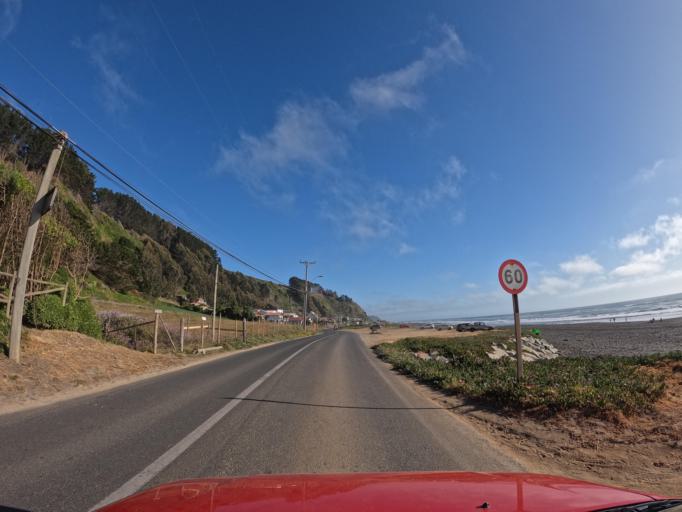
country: CL
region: Maule
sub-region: Provincia de Talca
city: Constitucion
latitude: -34.9093
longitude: -72.1815
